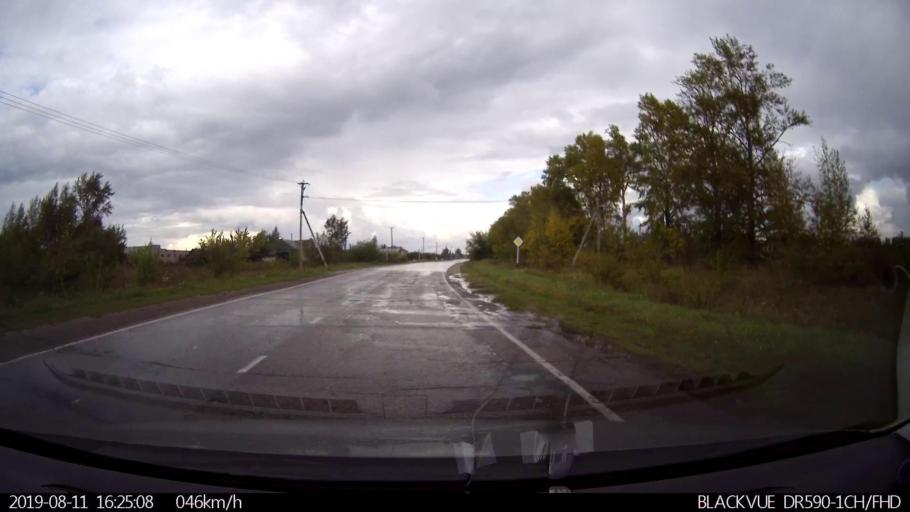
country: RU
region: Ulyanovsk
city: Mayna
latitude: 54.1044
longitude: 47.6013
